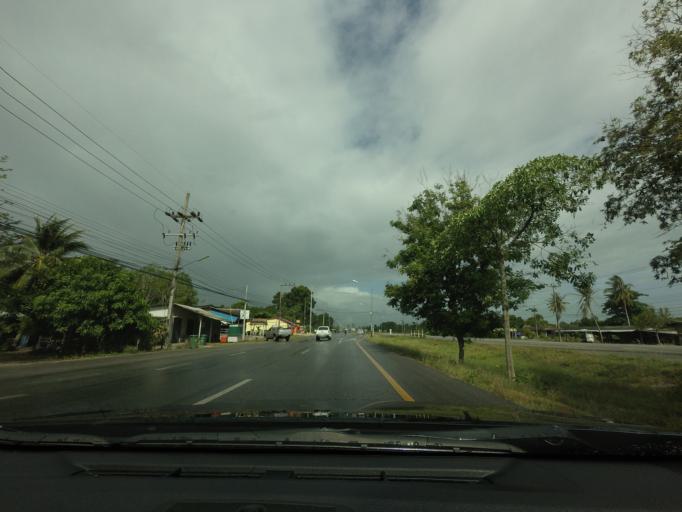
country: TH
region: Pattani
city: Nong Chik
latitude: 6.8057
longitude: 101.1293
